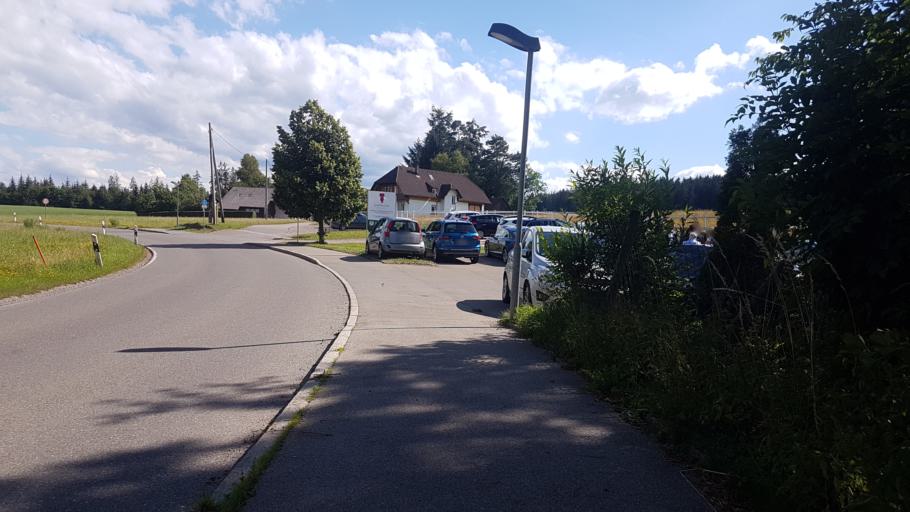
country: DE
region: Baden-Wuerttemberg
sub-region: Freiburg Region
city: Konigsfeld im Schwarzwald
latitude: 48.1418
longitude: 8.4026
